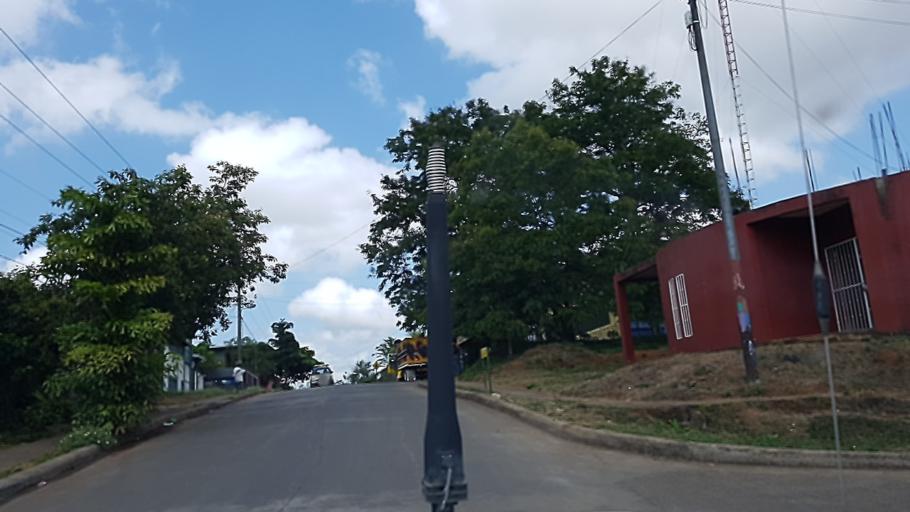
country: NI
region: Atlantico Sur
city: Nueva Guinea
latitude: 11.6874
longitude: -84.4534
